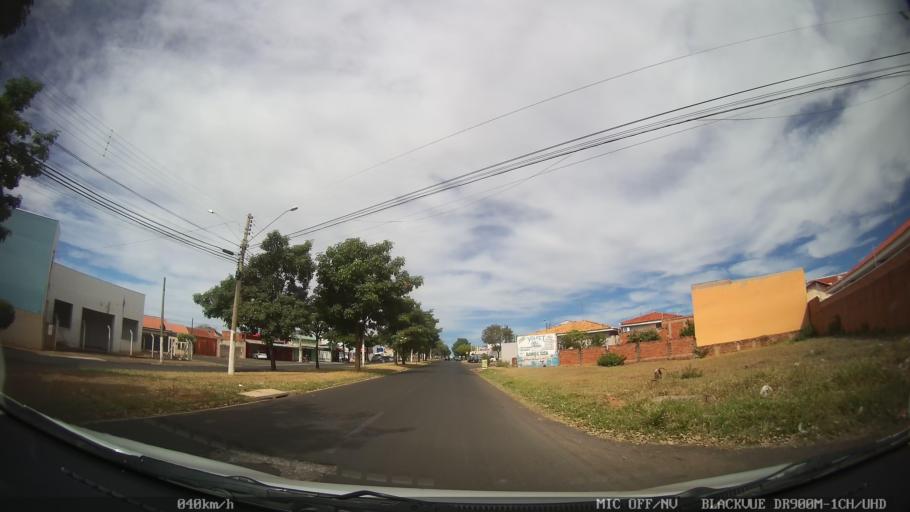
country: BR
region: Sao Paulo
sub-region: Catanduva
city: Catanduva
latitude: -21.1628
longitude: -48.9701
